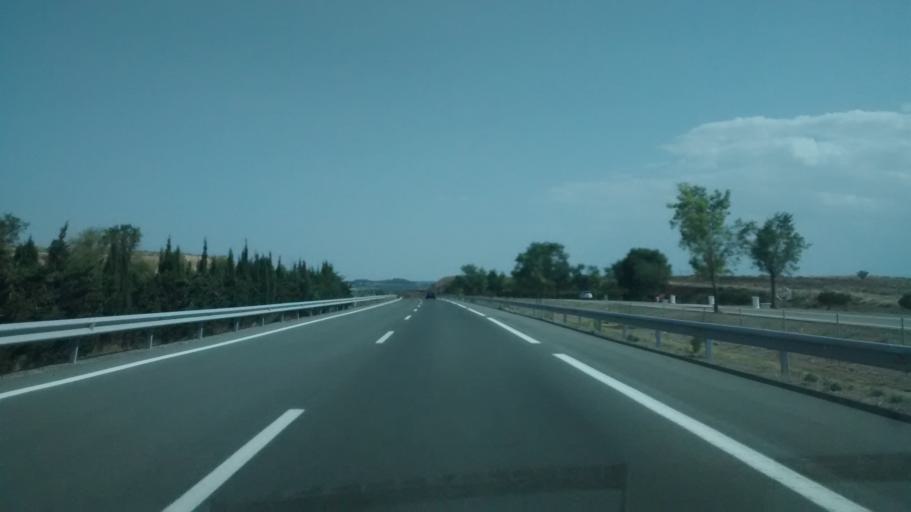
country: ES
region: Navarre
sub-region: Provincia de Navarra
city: Corella
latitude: 42.1650
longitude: -1.8268
